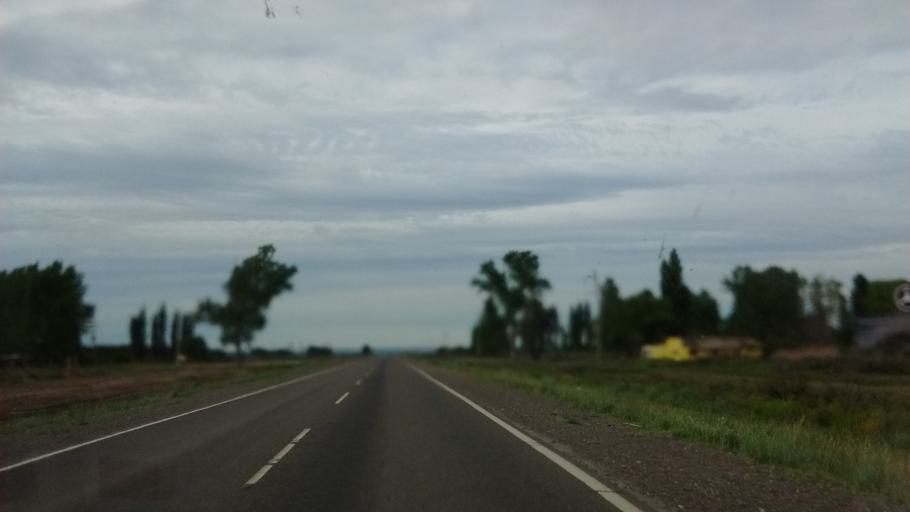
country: AR
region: Rio Negro
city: Catriel
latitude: -37.9212
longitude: -67.8737
